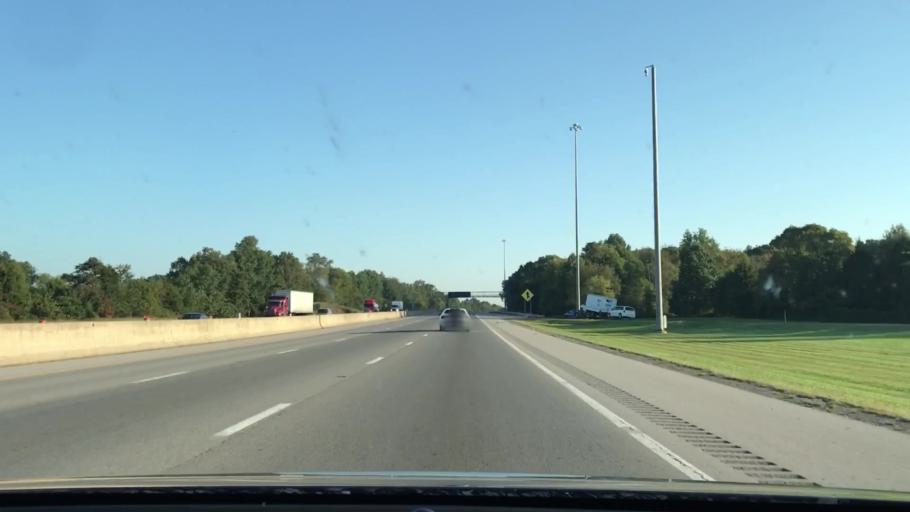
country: US
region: Kentucky
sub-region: Simpson County
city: Franklin
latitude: 36.6454
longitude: -86.5691
